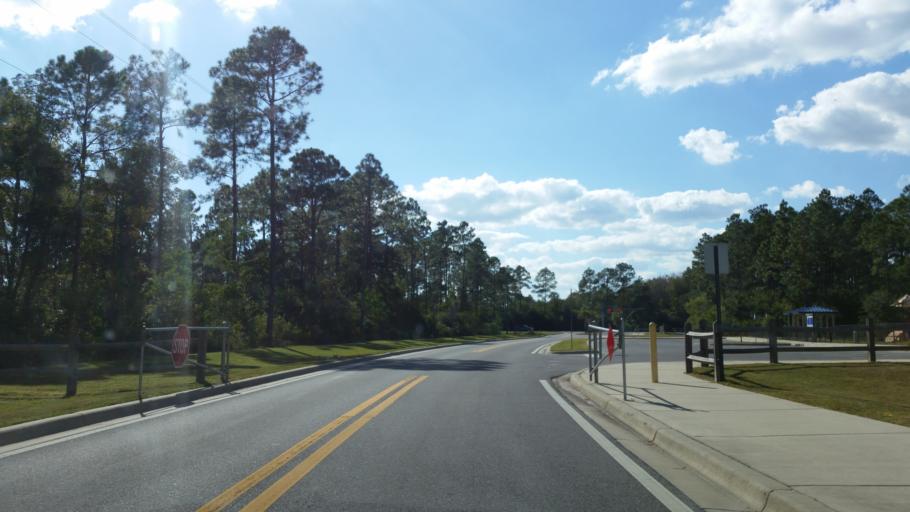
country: US
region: Florida
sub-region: Escambia County
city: Myrtle Grove
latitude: 30.3846
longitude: -87.4002
